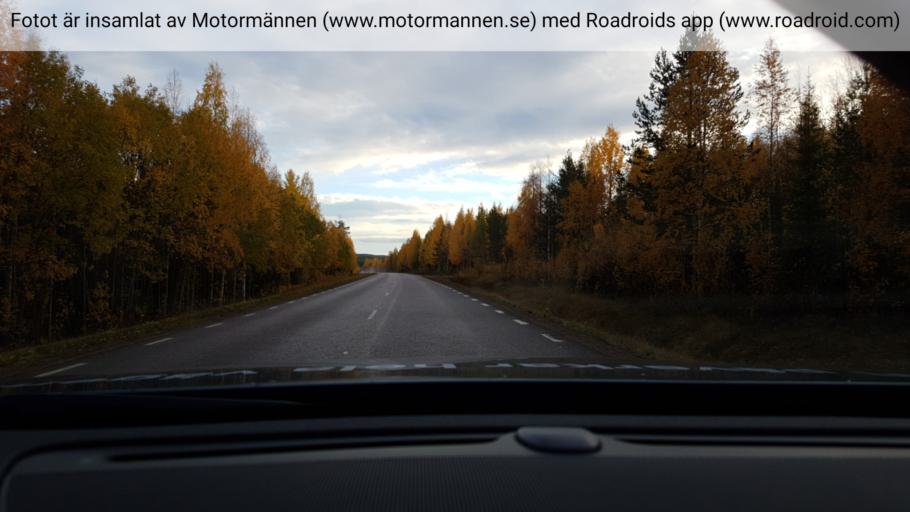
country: SE
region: Norrbotten
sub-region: Overkalix Kommun
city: OEverkalix
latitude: 66.8407
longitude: 22.7563
